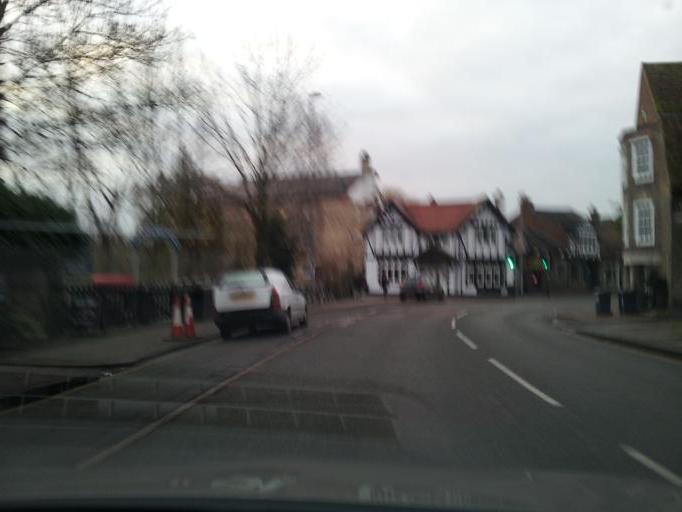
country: GB
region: England
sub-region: Cambridgeshire
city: Cambridge
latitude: 52.1998
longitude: 0.1136
